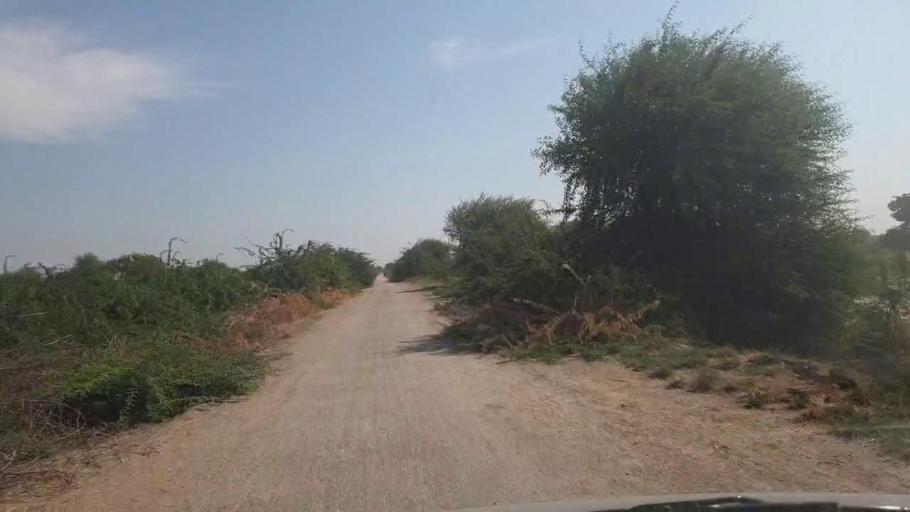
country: PK
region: Sindh
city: Digri
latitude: 24.9588
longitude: 69.1322
